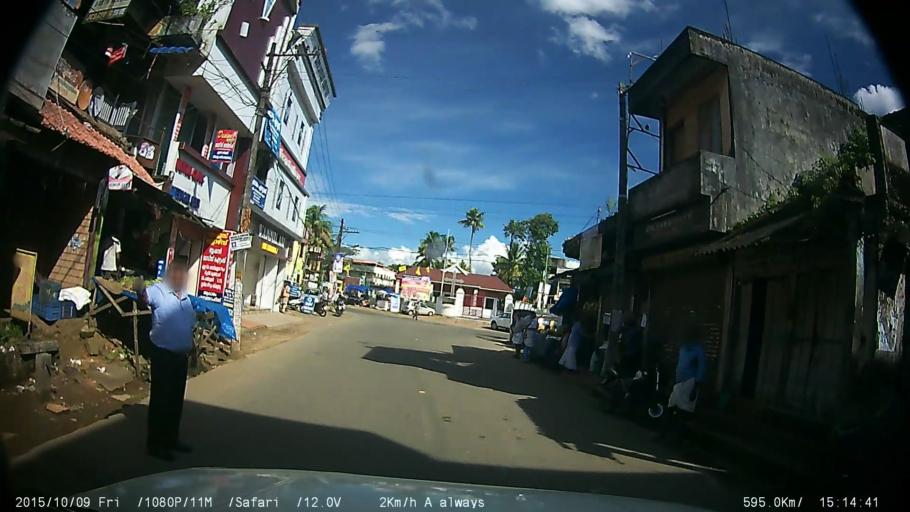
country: IN
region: Kerala
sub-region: Ernakulam
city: Piravam
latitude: 9.8618
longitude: 76.5951
